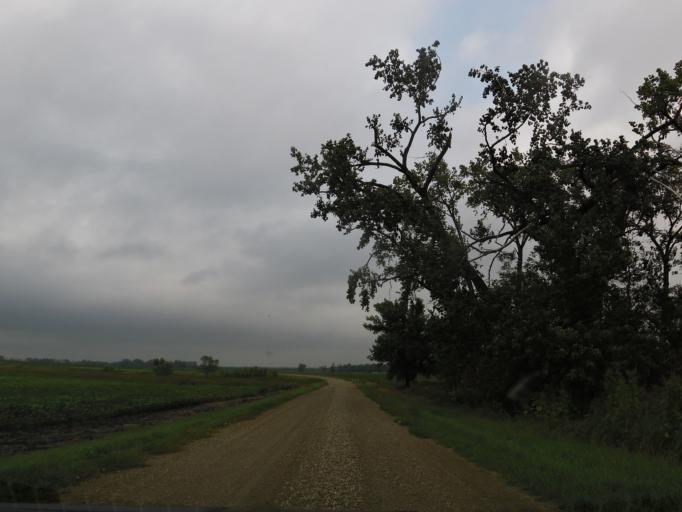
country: US
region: North Dakota
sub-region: Walsh County
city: Grafton
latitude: 48.4527
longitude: -97.1690
